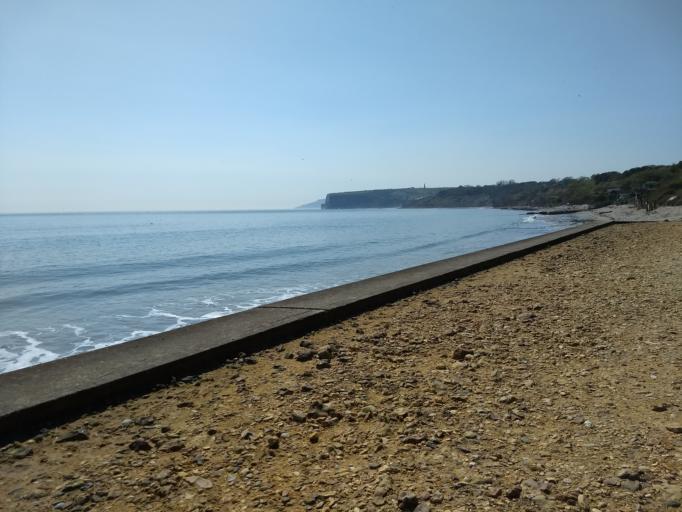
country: GB
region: England
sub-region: Isle of Wight
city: Bembridge
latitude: 50.6813
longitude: -1.0746
